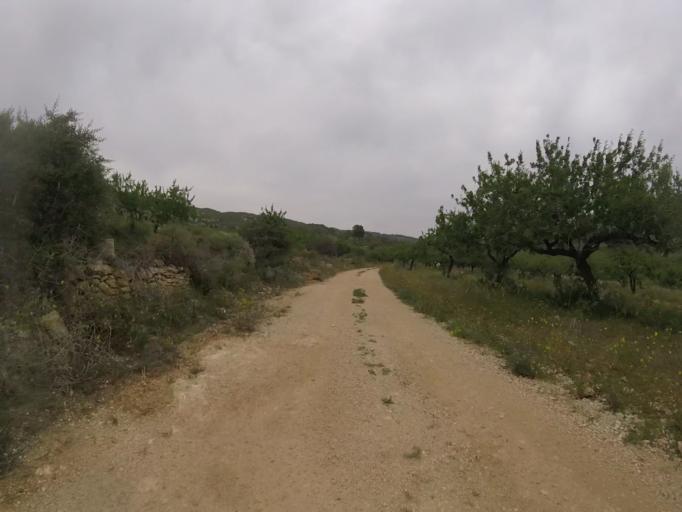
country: ES
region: Valencia
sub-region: Provincia de Castello
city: Alcala de Xivert
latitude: 40.2864
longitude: 0.2574
